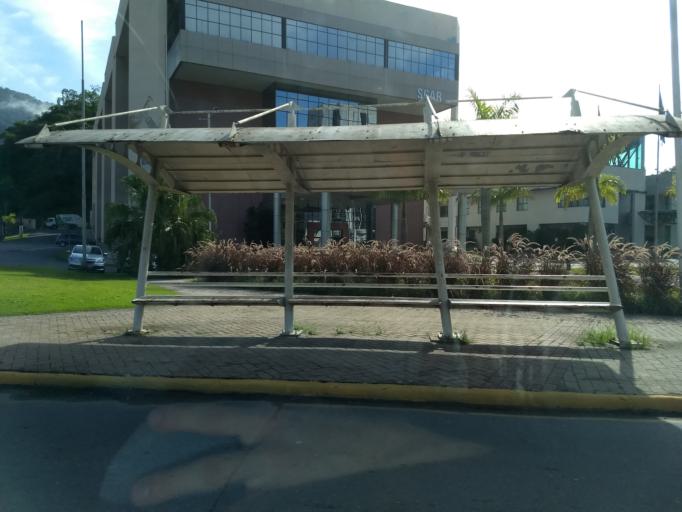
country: BR
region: Santa Catarina
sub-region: Jaragua Do Sul
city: Jaragua do Sul
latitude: -26.4781
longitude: -49.0812
